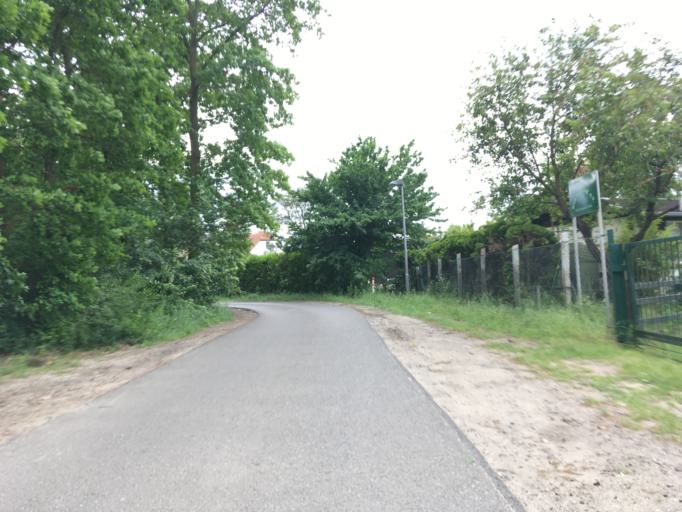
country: DE
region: Berlin
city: Biesdorf
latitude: 52.4825
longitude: 13.5679
